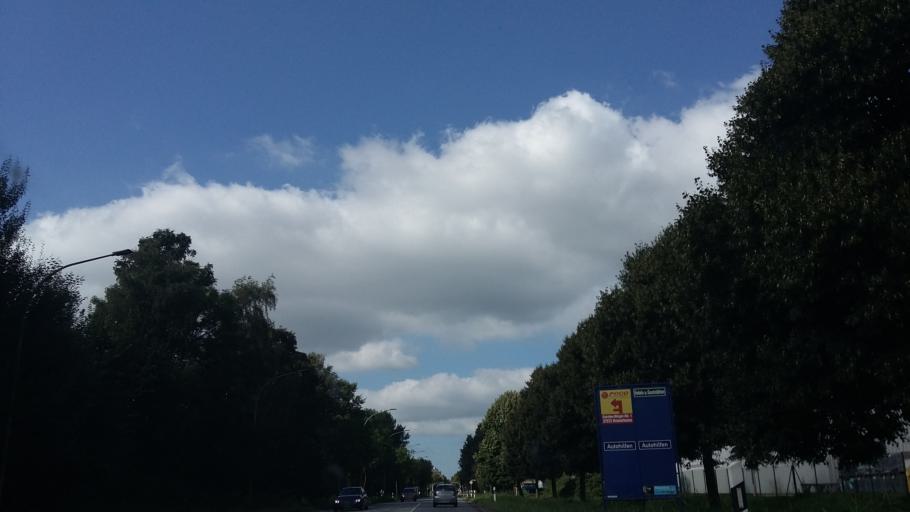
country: DE
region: Lower Saxony
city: Loxstedt
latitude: 53.4923
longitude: 8.6022
